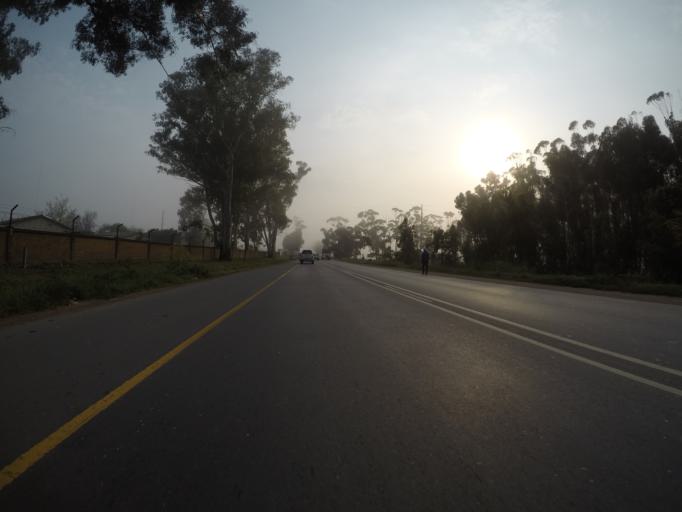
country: ZA
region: Western Cape
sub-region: City of Cape Town
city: Kraaifontein
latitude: -33.7946
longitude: 18.6940
